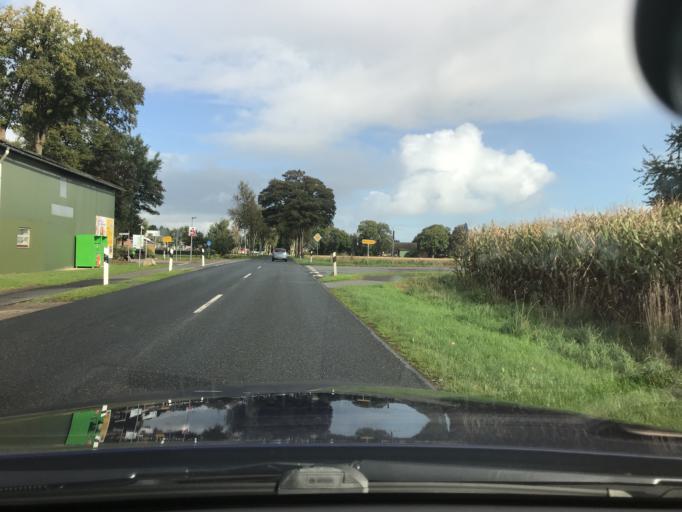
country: DE
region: Lower Saxony
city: Hammah
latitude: 53.6030
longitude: 9.3666
